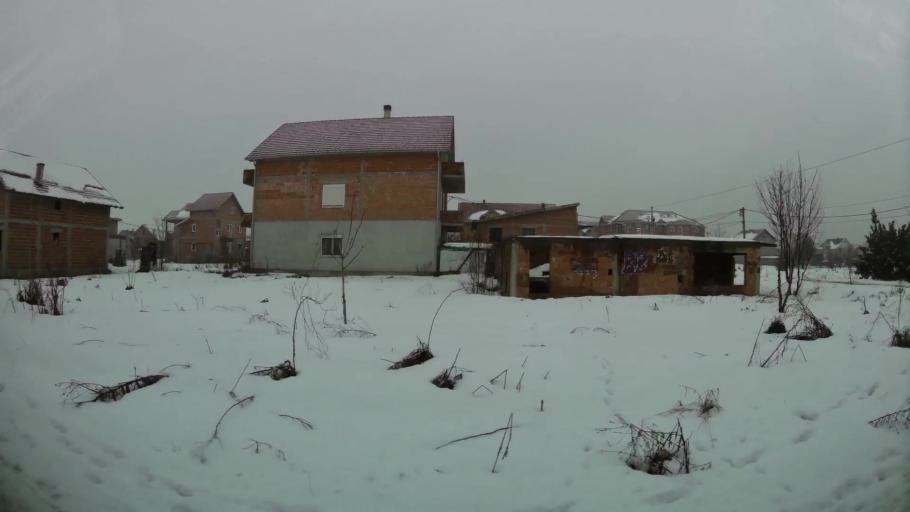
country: RS
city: Novi Banovci
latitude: 44.8745
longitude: 20.3123
